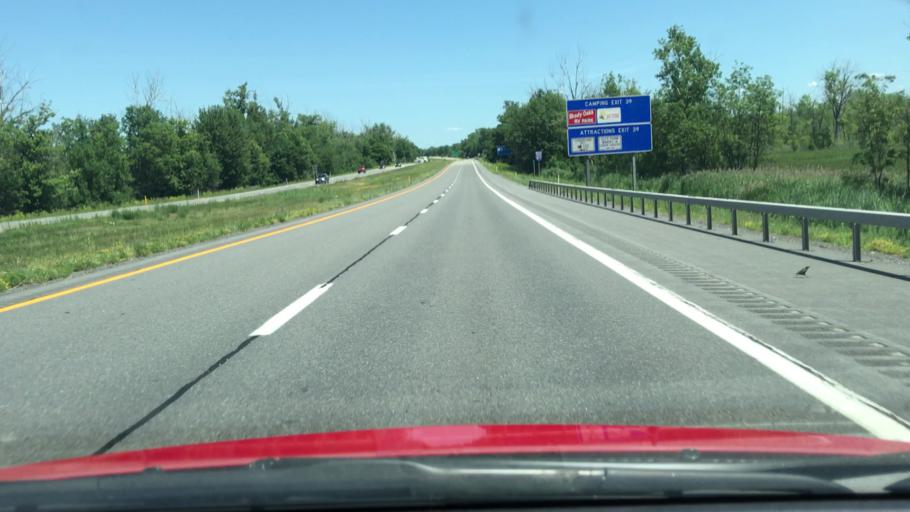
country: US
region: New York
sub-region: Clinton County
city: Plattsburgh
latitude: 44.7189
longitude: -73.4551
